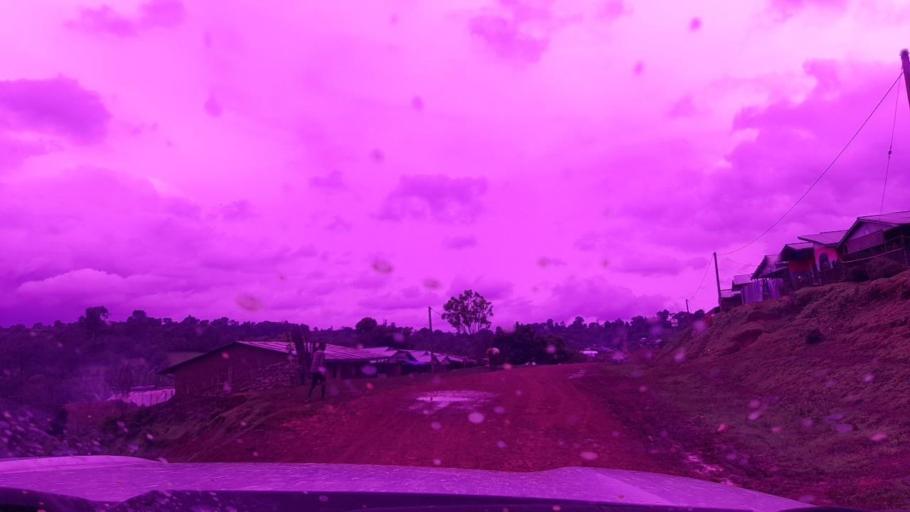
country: ET
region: Southern Nations, Nationalities, and People's Region
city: Tippi
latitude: 7.5680
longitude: 35.6608
